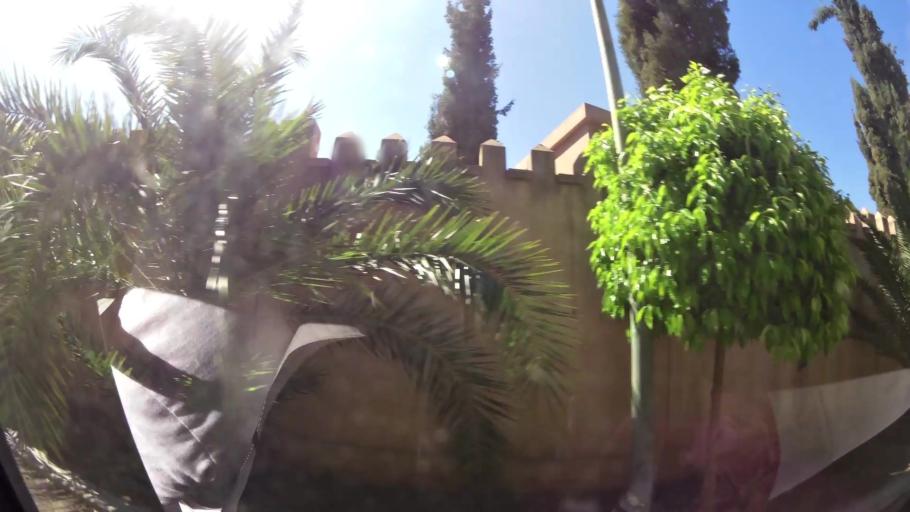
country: MA
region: Marrakech-Tensift-Al Haouz
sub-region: Marrakech
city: Marrakesh
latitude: 31.6603
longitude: -7.9604
